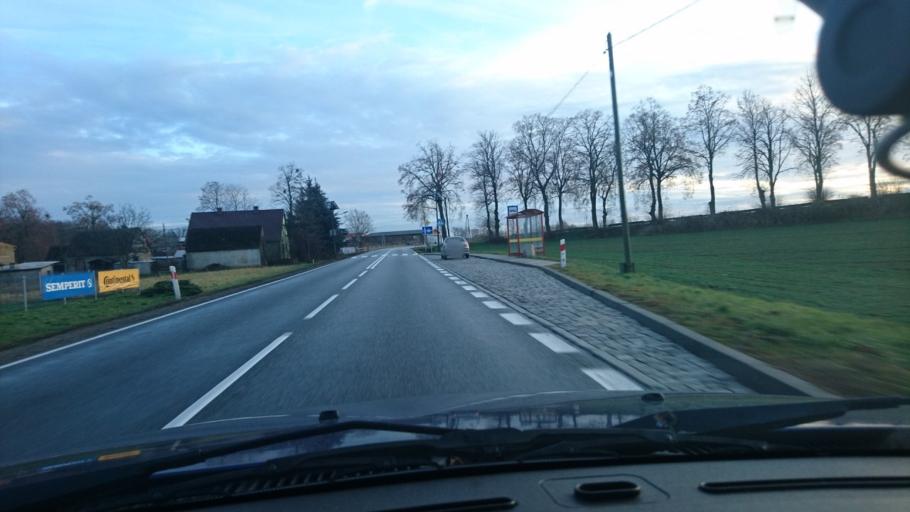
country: PL
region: Opole Voivodeship
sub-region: Powiat kluczborski
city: Byczyna
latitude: 51.1368
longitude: 18.1982
